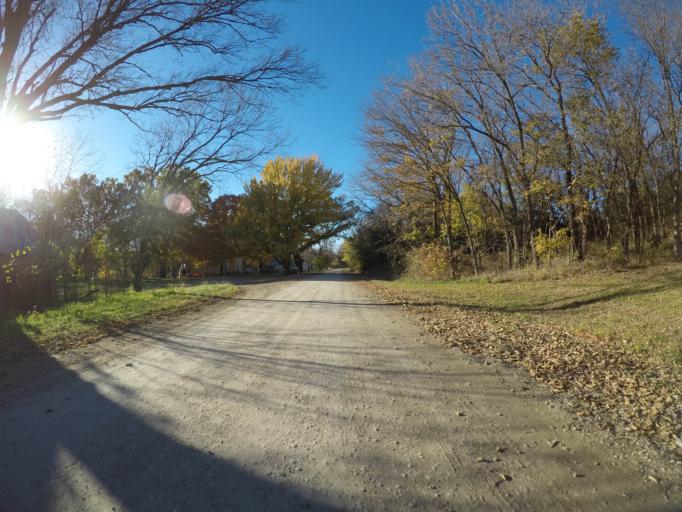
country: US
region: Kansas
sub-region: Riley County
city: Fort Riley North
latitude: 39.2643
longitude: -96.7804
